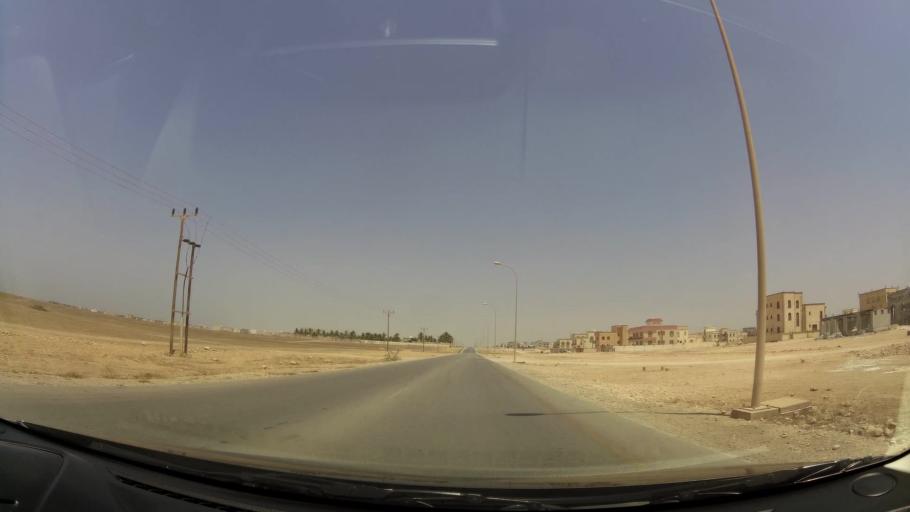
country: OM
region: Zufar
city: Salalah
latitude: 17.0685
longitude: 54.2030
